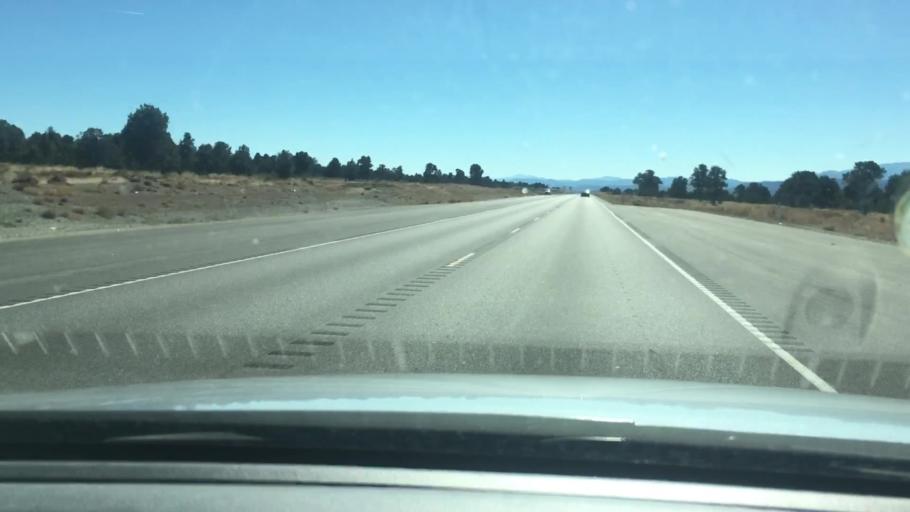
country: US
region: Nevada
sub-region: White Pine County
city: Ely
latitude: 39.1849
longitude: -115.0099
